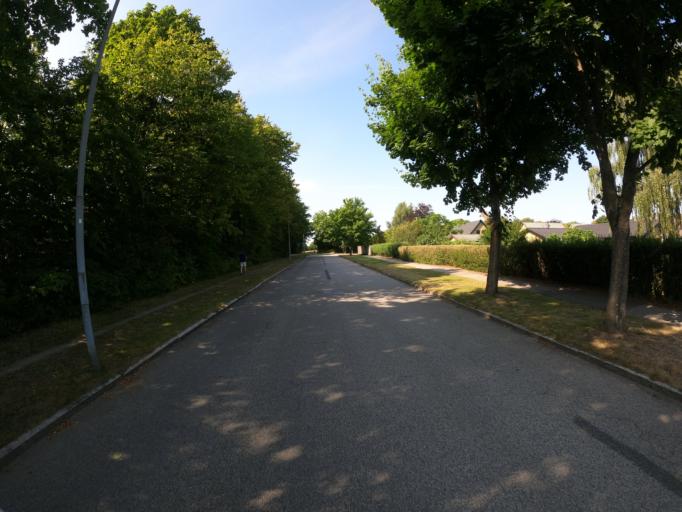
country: SE
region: Skane
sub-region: Lunds Kommun
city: Lund
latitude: 55.7298
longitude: 13.1659
